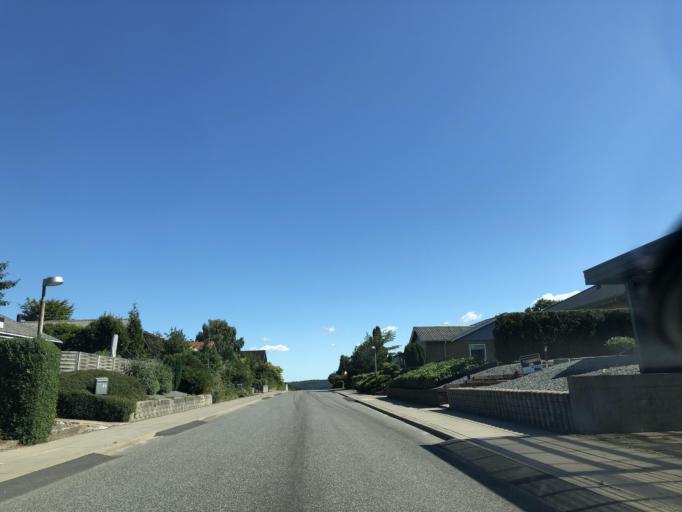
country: DK
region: North Denmark
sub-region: Mariagerfjord Kommune
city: Hobro
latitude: 56.6442
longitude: 9.8015
